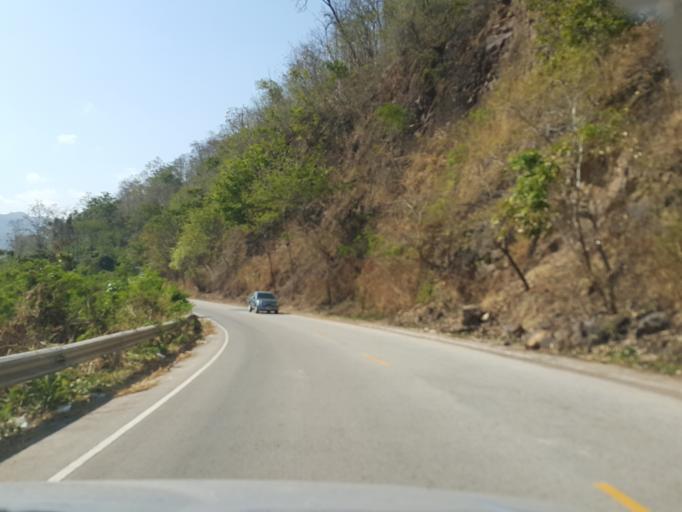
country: TH
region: Chiang Mai
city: Mae Wang
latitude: 18.6173
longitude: 98.7545
